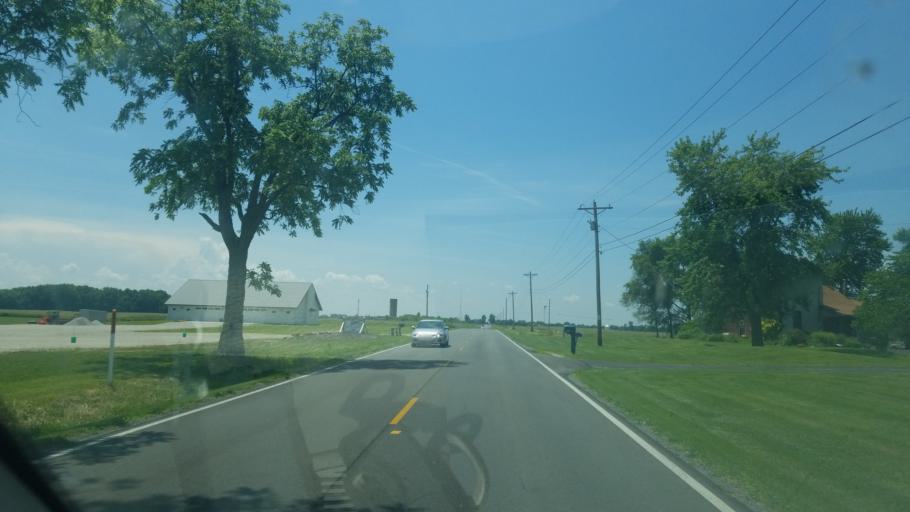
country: US
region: Ohio
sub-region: Hancock County
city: Findlay
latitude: 41.0894
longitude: -83.6131
